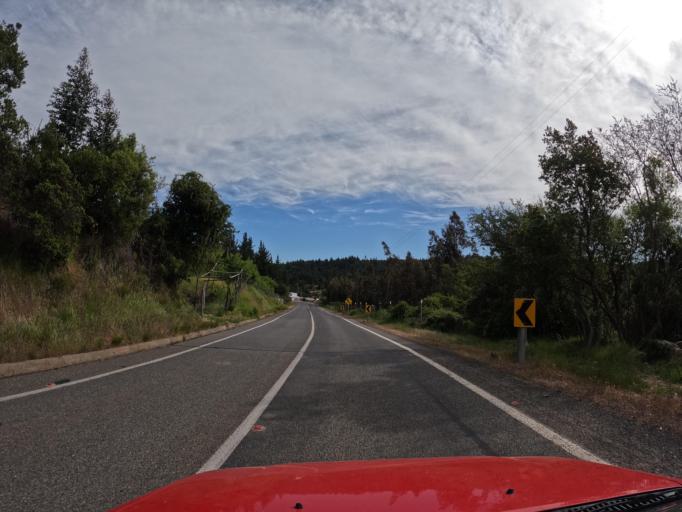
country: CL
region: Maule
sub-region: Provincia de Talca
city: Talca
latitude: -35.3028
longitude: -71.9639
